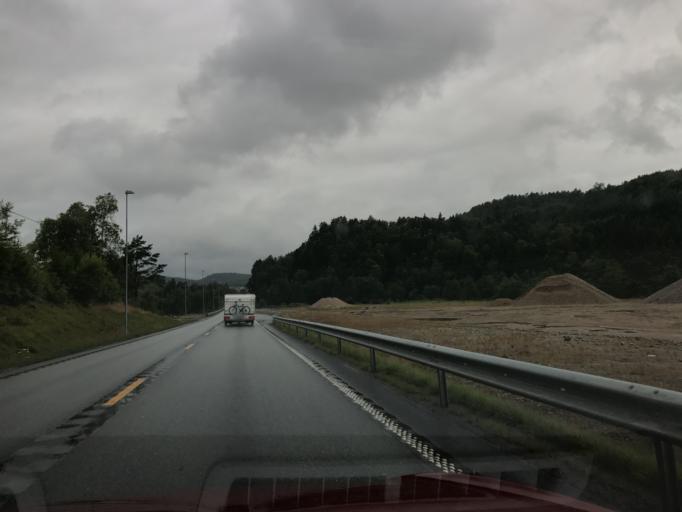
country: NO
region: Vest-Agder
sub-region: Lyngdal
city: Lyngdal
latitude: 58.1540
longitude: 7.1343
